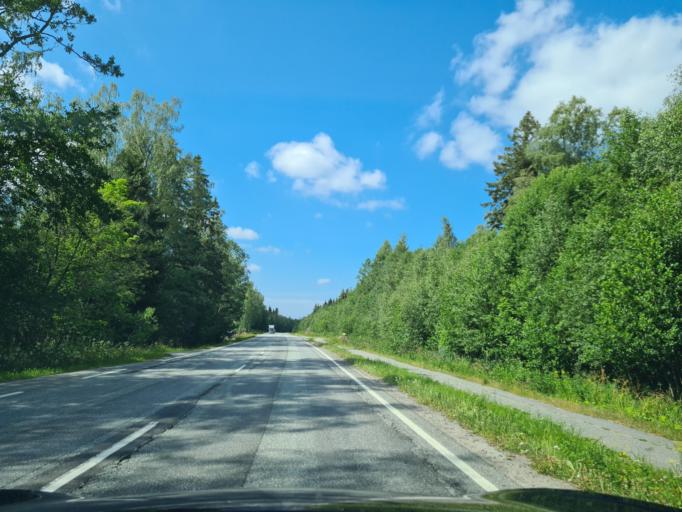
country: FI
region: Ostrobothnia
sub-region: Vaasa
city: Vaasa
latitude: 63.1976
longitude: 21.5418
